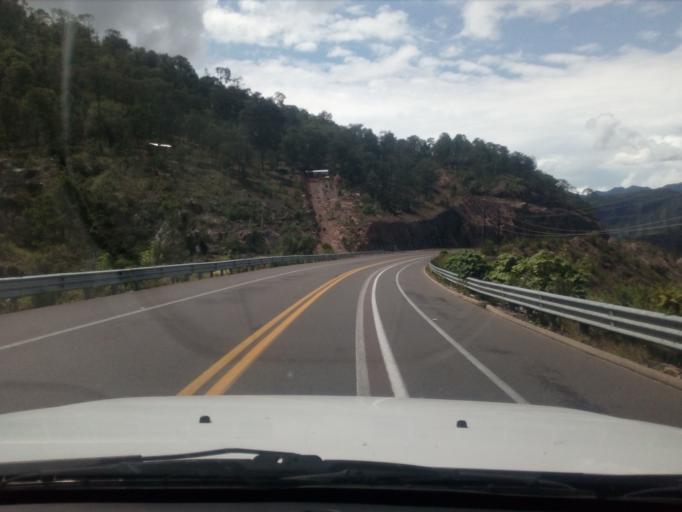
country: MX
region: Durango
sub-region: Pueblo Nuevo
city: La Ciudad
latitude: 23.6224
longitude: -105.6791
